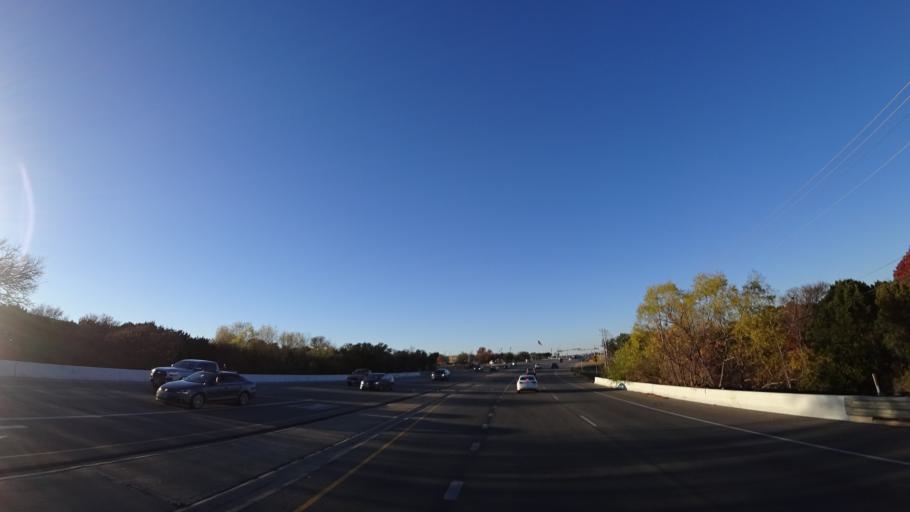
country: US
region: Texas
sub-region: Williamson County
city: Brushy Creek
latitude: 30.5317
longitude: -97.7809
